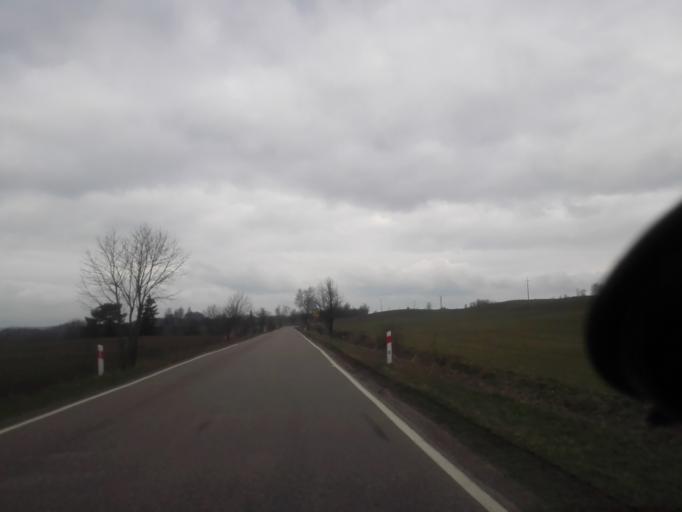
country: PL
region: Podlasie
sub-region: Suwalki
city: Suwalki
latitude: 54.2303
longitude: 22.9126
